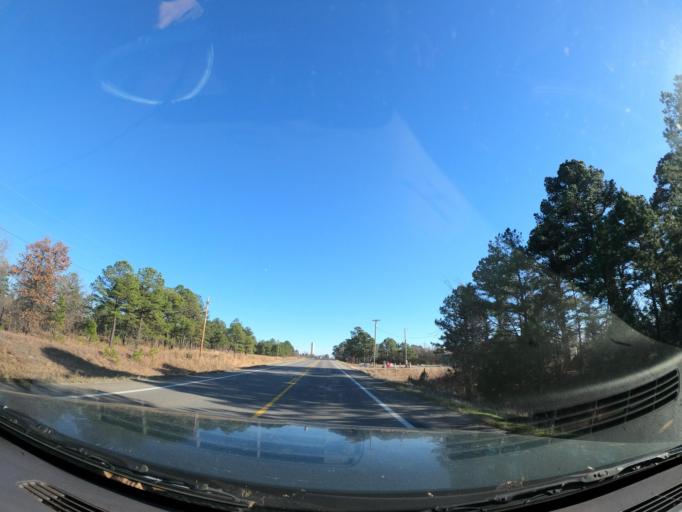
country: US
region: Oklahoma
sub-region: Pittsburg County
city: Longtown
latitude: 35.2313
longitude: -95.4560
